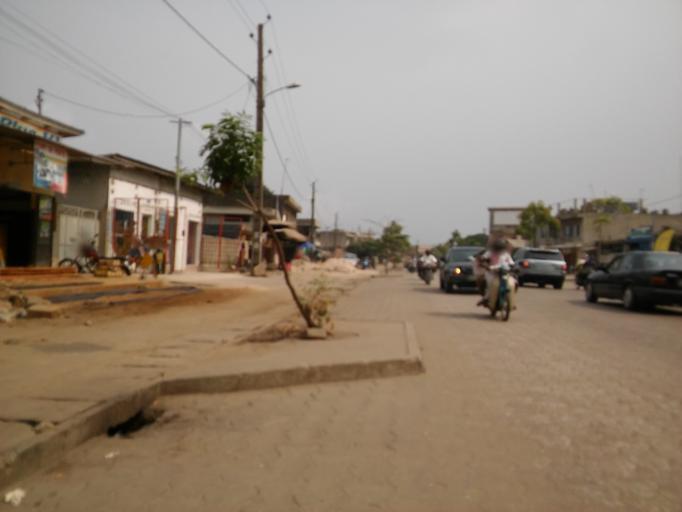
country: BJ
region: Littoral
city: Cotonou
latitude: 6.3884
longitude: 2.3860
